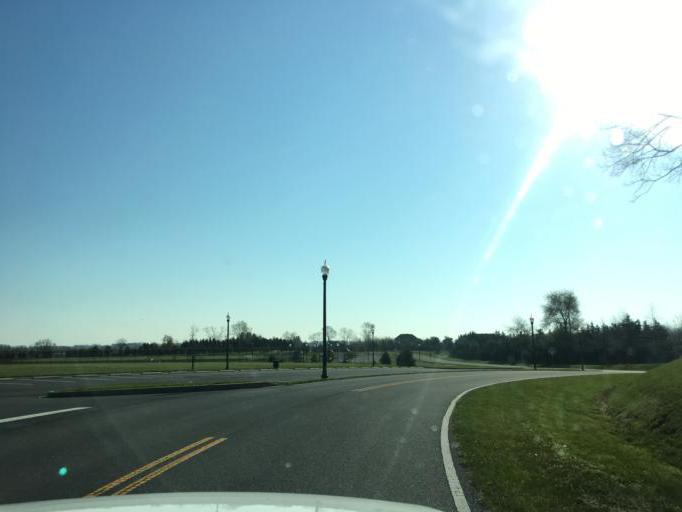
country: US
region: Maryland
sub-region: Frederick County
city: Walkersville
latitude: 39.5118
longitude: -77.4040
